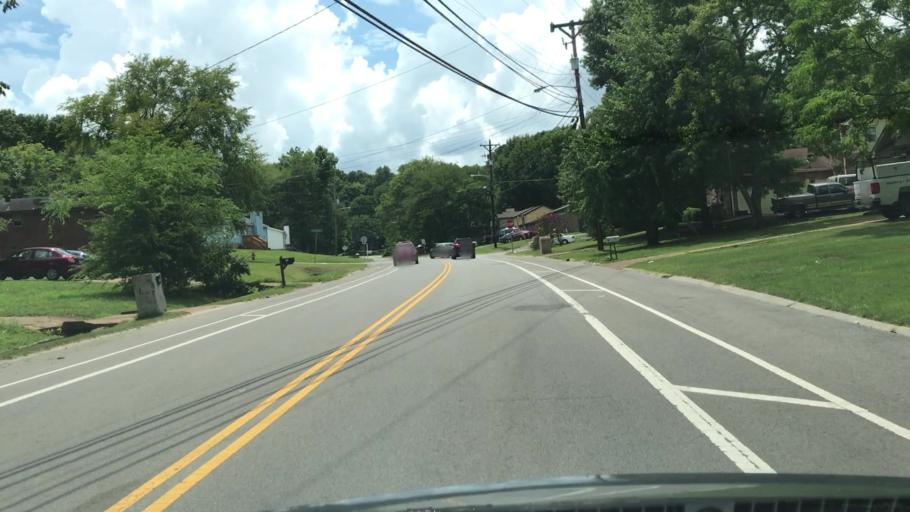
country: US
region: Tennessee
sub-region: Williamson County
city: Brentwood Estates
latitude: 36.0408
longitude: -86.7045
